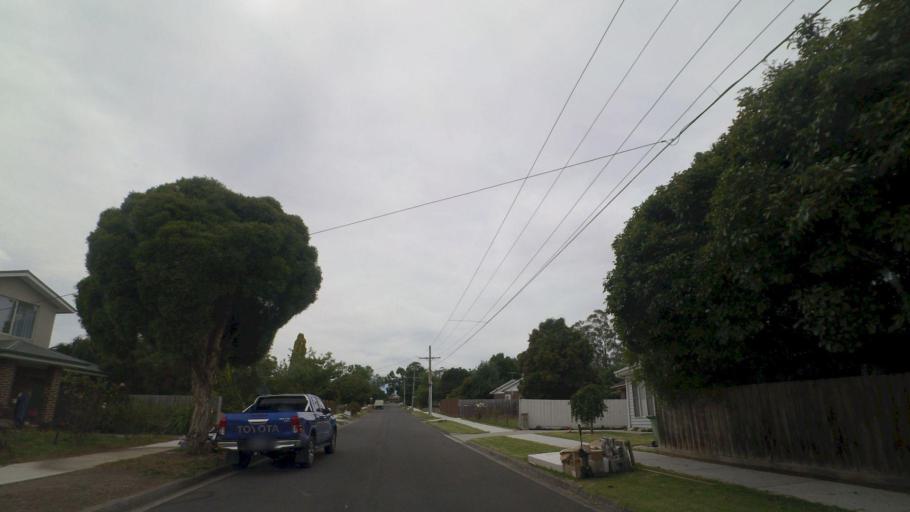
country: AU
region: Victoria
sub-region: Yarra Ranges
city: Kilsyth
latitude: -37.7826
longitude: 145.3329
